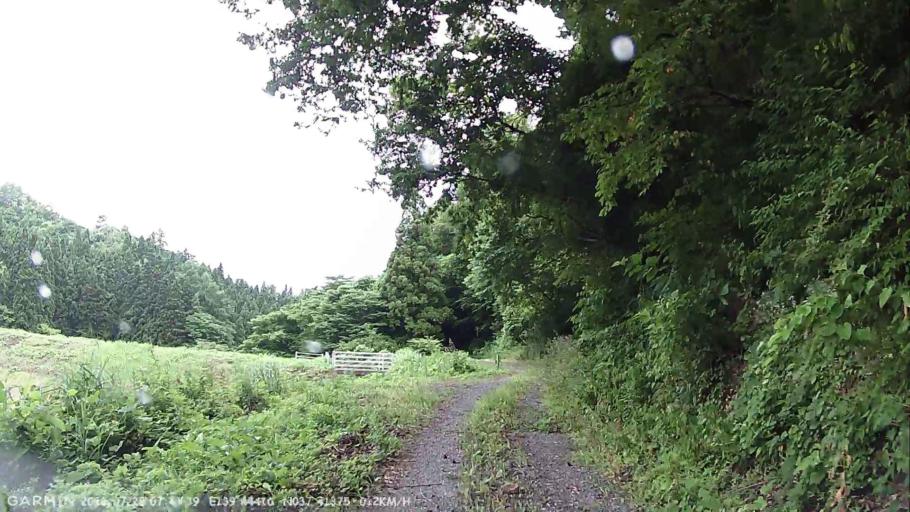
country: JP
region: Fukushima
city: Kitakata
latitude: 37.4138
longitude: 139.8440
